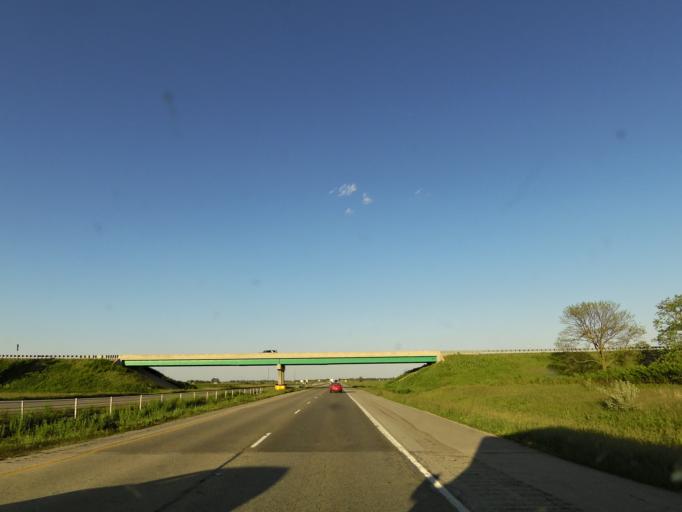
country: US
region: Illinois
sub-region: Champaign County
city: Homer
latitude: 40.1237
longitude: -87.9037
